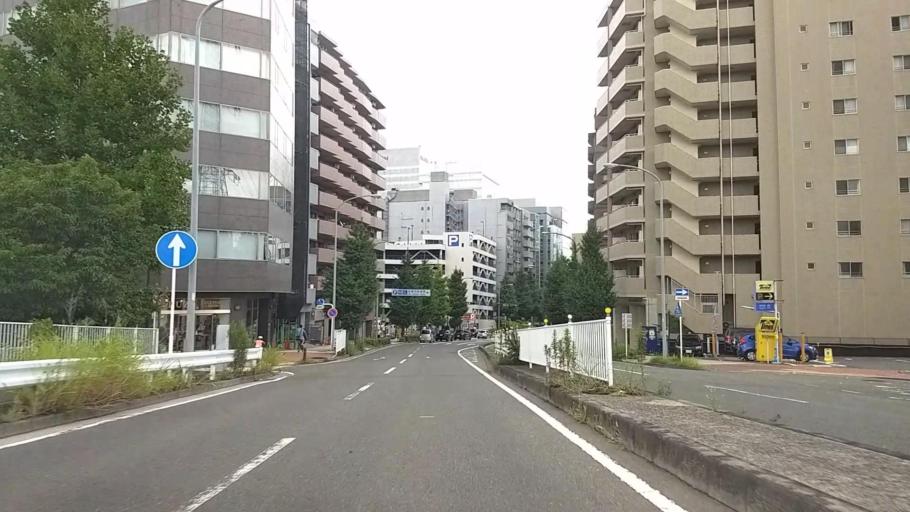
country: JP
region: Kanagawa
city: Yokohama
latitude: 35.5125
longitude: 139.6169
